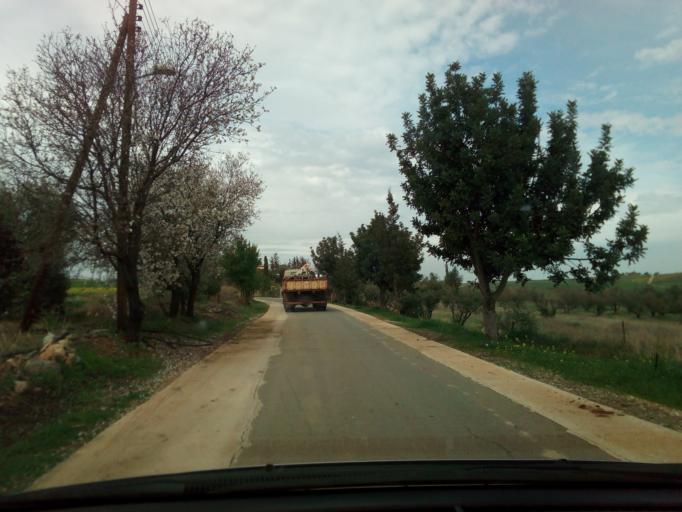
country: CY
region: Lefkosia
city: Astromeritis
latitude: 35.1040
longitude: 32.9744
